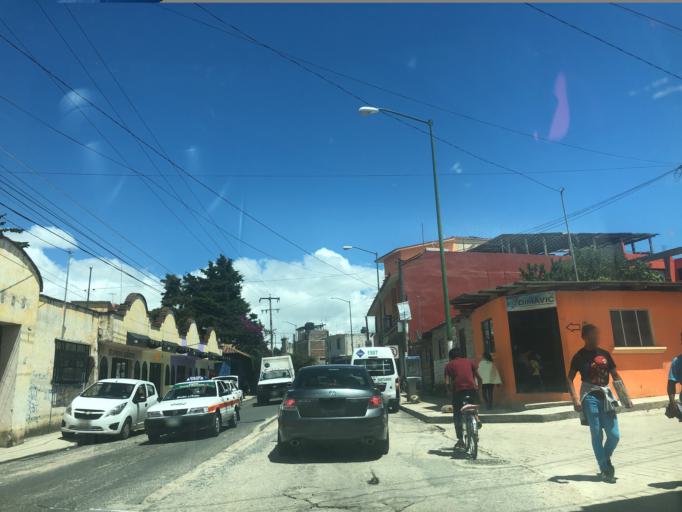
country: MX
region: Chiapas
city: San Cristobal de las Casas
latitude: 16.7176
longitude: -92.6403
